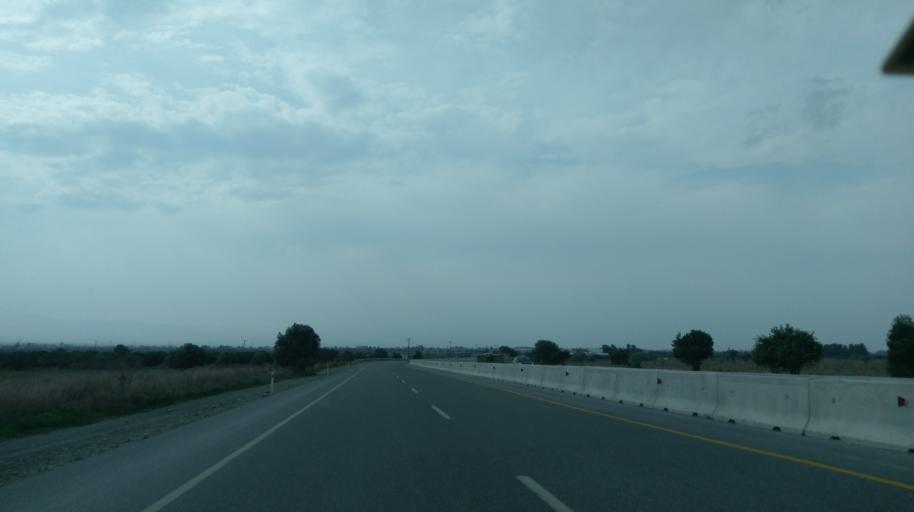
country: CY
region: Lefkosia
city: Morfou
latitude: 35.2018
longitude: 33.0357
